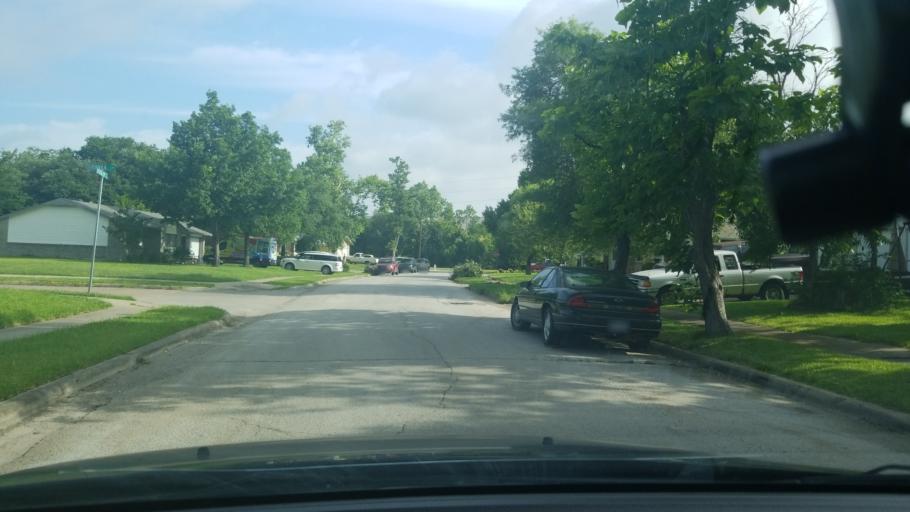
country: US
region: Texas
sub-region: Dallas County
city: Mesquite
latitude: 32.7719
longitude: -96.6297
